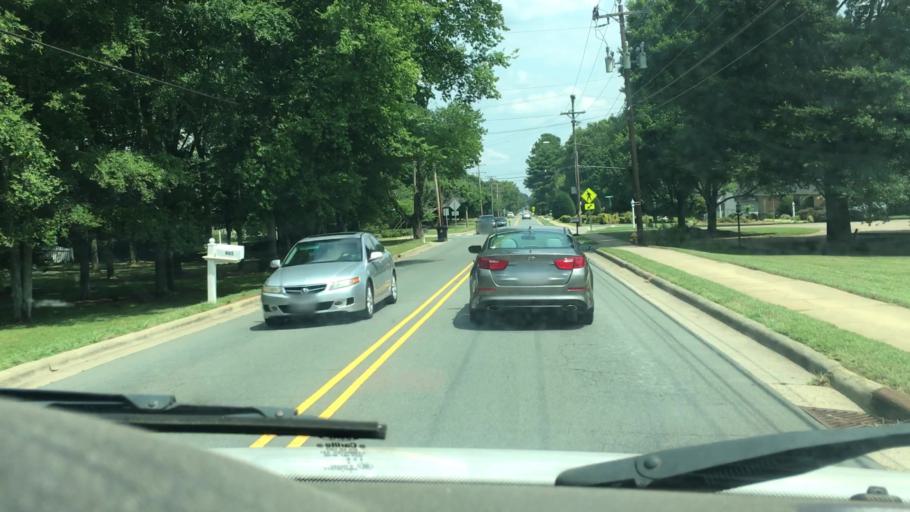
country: US
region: North Carolina
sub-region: Gaston County
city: Davidson
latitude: 35.4916
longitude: -80.8321
